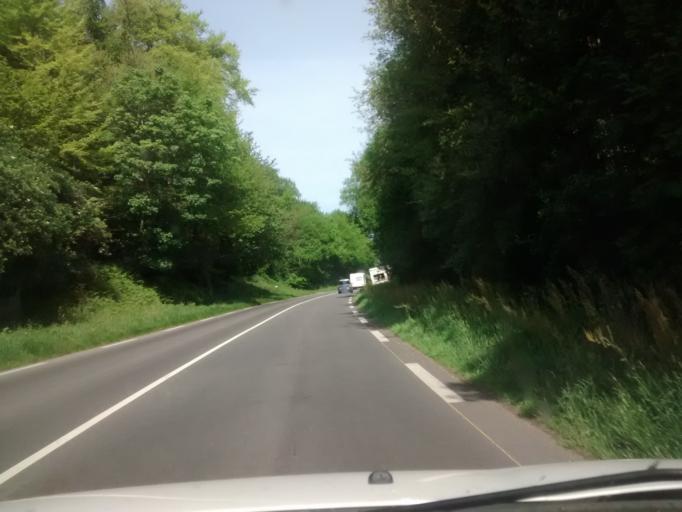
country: FR
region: Brittany
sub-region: Departement d'Ille-et-Vilaine
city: Antrain
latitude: 48.4623
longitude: -1.5055
